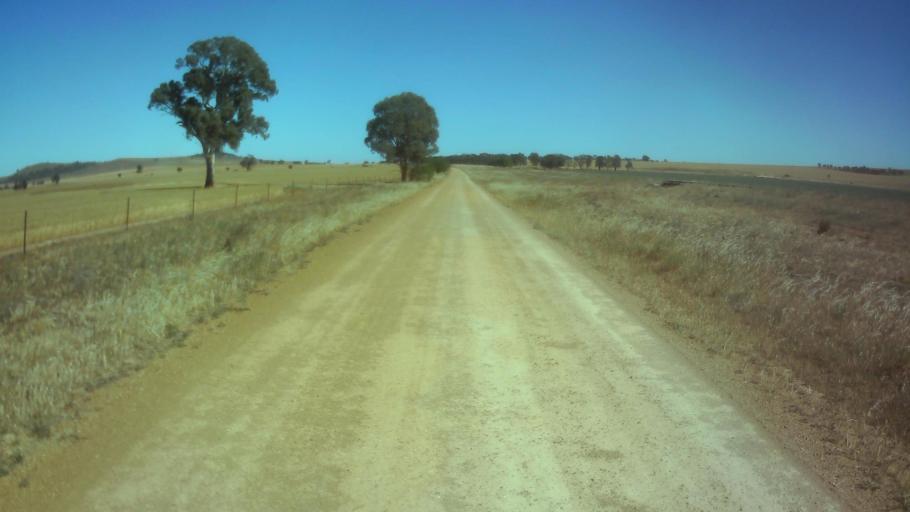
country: AU
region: New South Wales
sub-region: Weddin
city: Grenfell
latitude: -33.9736
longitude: 148.3207
